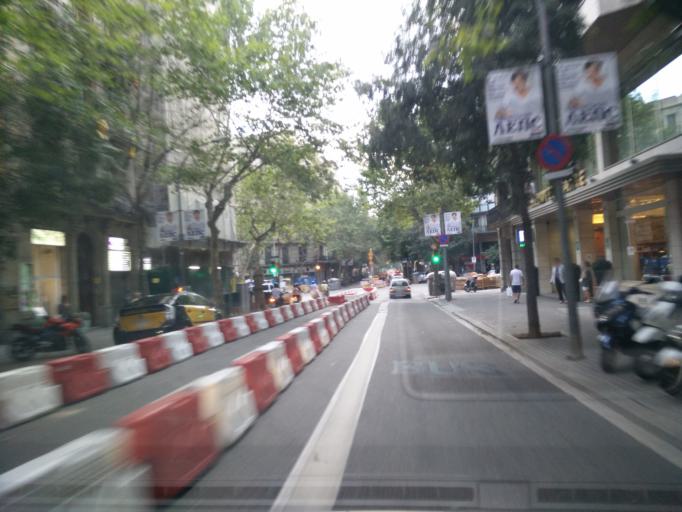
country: ES
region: Catalonia
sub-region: Provincia de Barcelona
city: Barcelona
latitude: 41.3895
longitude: 2.1568
